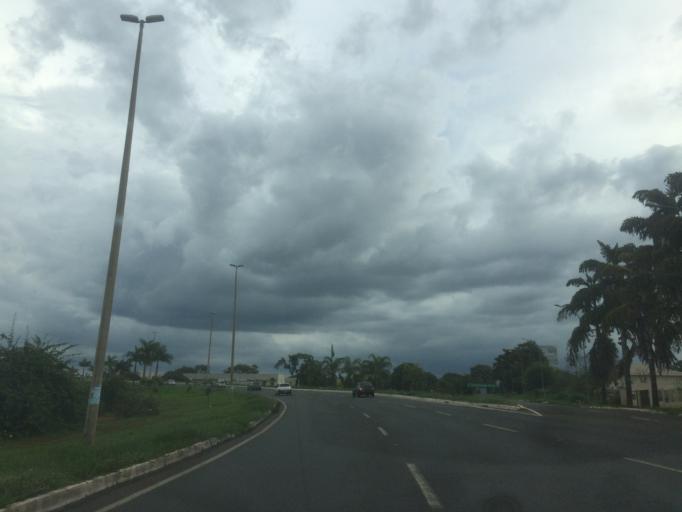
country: BR
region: Federal District
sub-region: Brasilia
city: Brasilia
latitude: -15.7902
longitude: -47.8589
